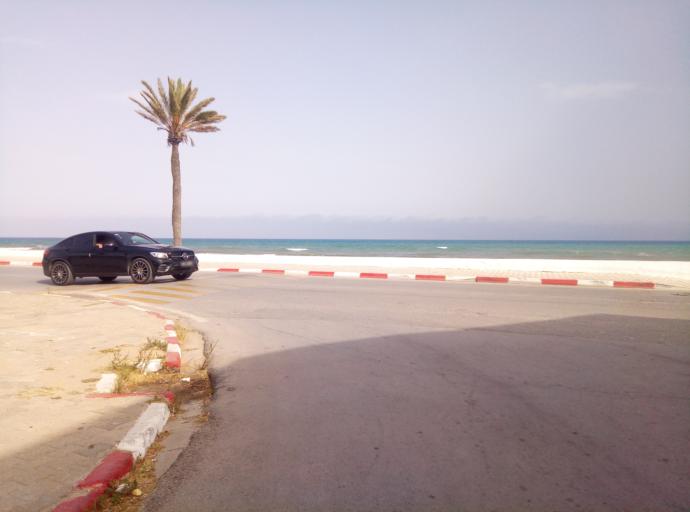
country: TN
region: Nabul
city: Al Hammamat
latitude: 36.3938
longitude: 10.6180
